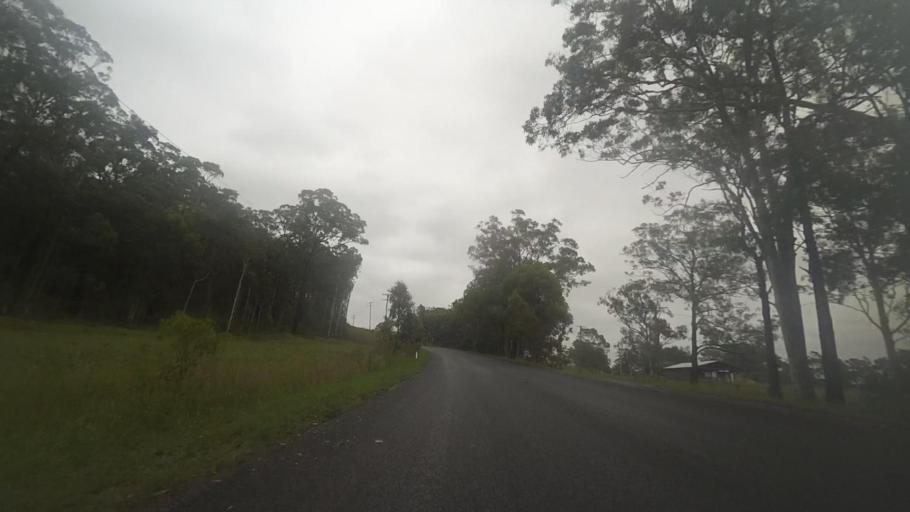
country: AU
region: New South Wales
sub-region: Port Stephens Shire
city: Port Stephens
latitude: -32.6491
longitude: 151.9748
